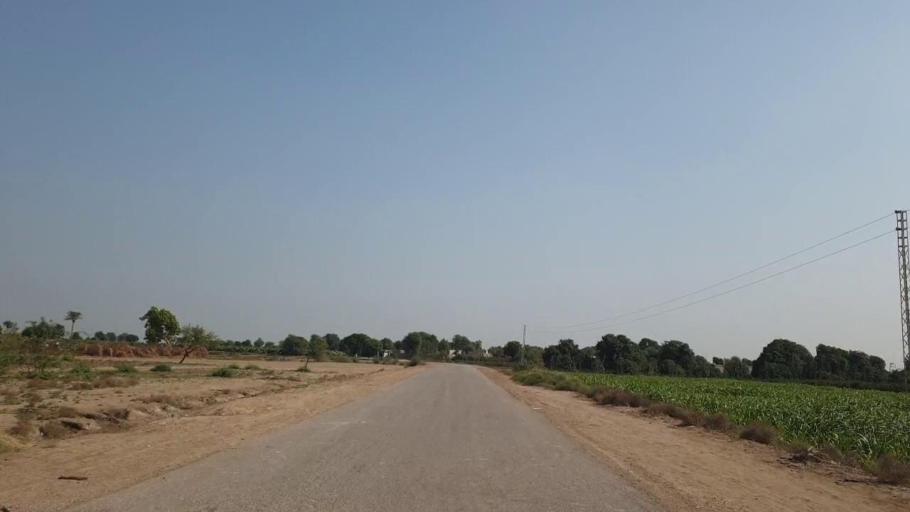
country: PK
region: Sindh
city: Matiari
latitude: 25.5015
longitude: 68.4413
